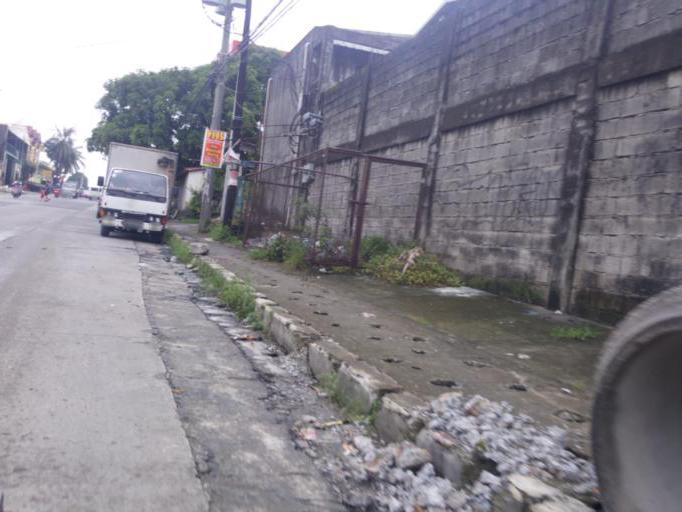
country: PH
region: Calabarzon
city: Bagong Pagasa
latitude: 14.7077
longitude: 121.0214
